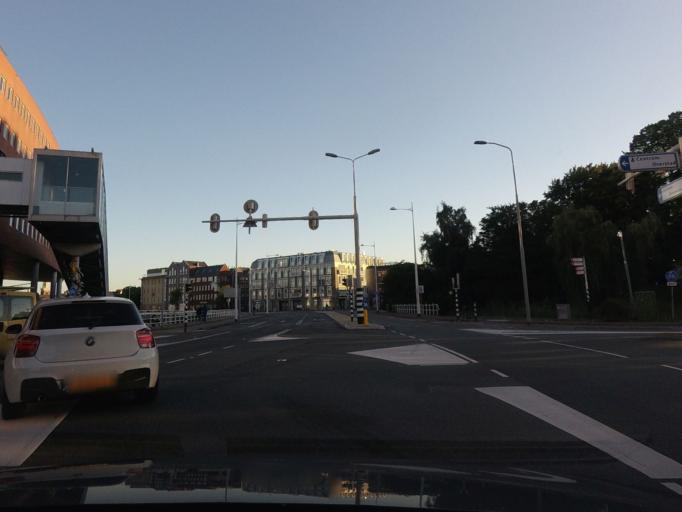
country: NL
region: North Holland
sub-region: Gemeente Alkmaar
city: Alkmaar
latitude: 52.6357
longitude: 4.7456
